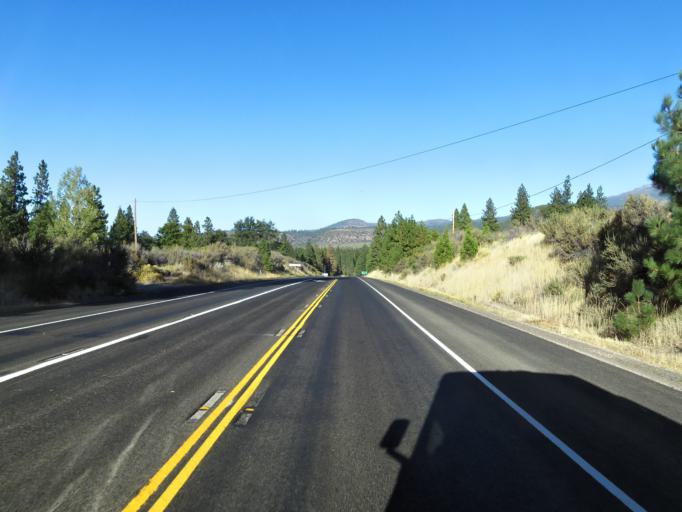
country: US
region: California
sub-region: Siskiyou County
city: Weed
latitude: 41.4441
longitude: -122.3723
